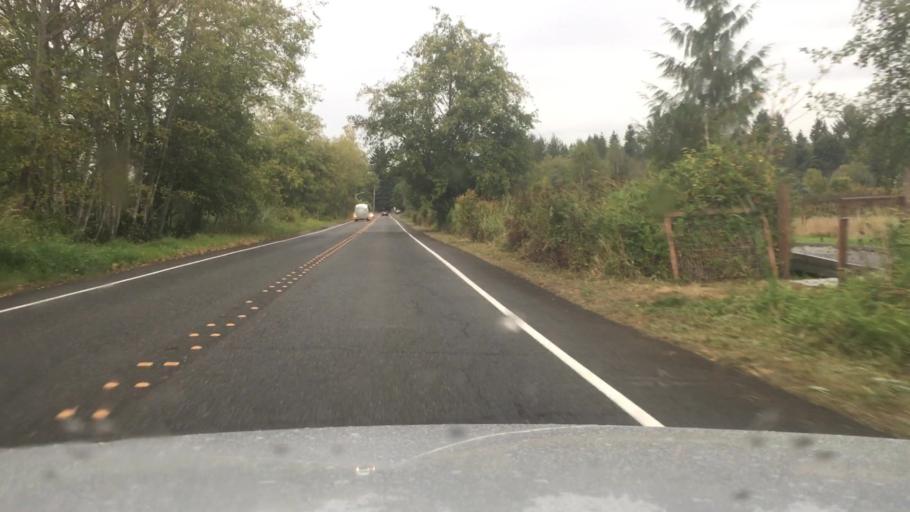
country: US
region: Washington
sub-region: King County
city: Eastgate
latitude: 47.5968
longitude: -122.1317
